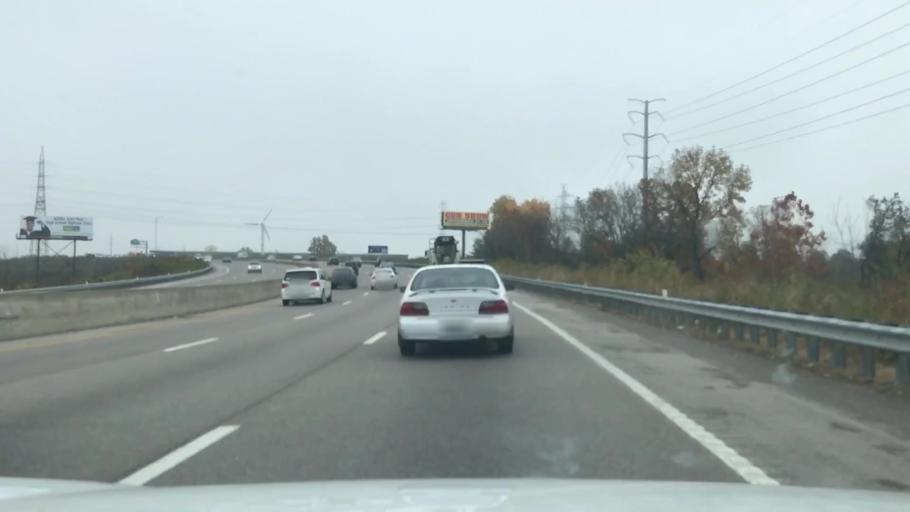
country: US
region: Missouri
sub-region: Saint Louis County
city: Vinita Park
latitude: 38.6814
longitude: -90.3563
